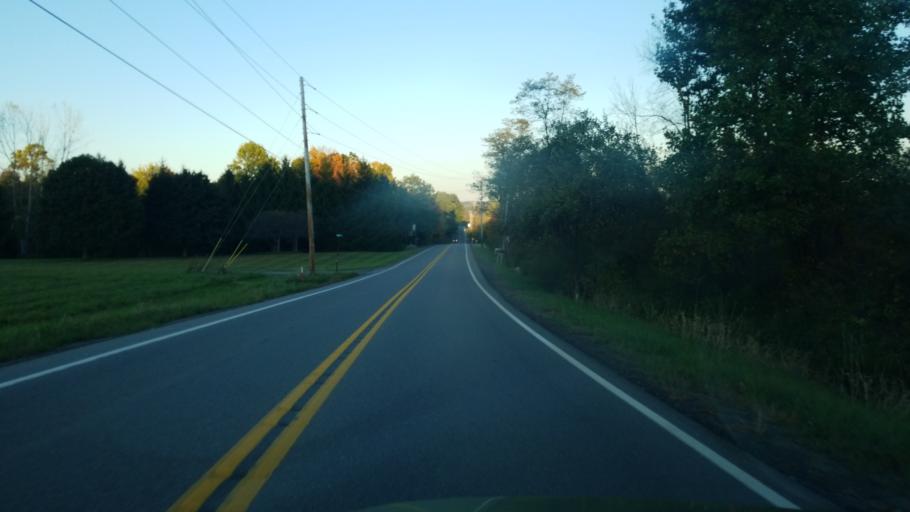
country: US
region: Pennsylvania
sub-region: Jefferson County
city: Reynoldsville
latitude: 41.0638
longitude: -78.9252
